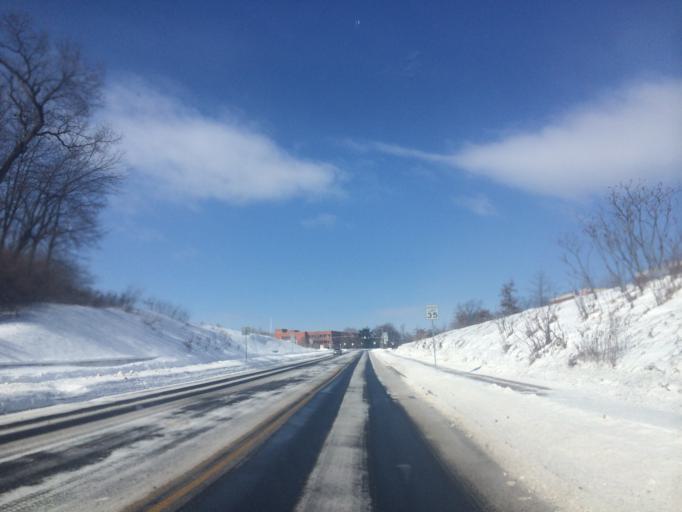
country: US
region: Pennsylvania
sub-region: Centre County
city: State College
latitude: 40.7740
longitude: -77.8902
